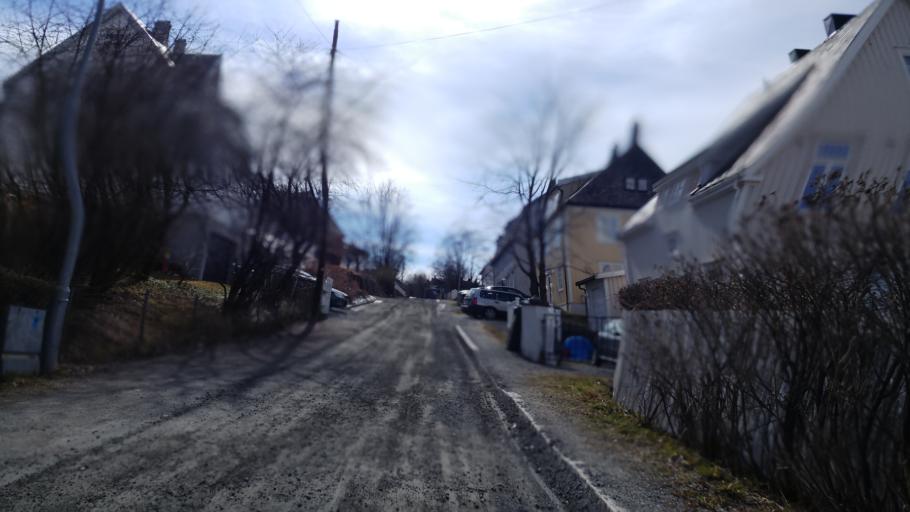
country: NO
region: Sor-Trondelag
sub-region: Trondheim
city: Trondheim
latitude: 63.4367
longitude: 10.4392
